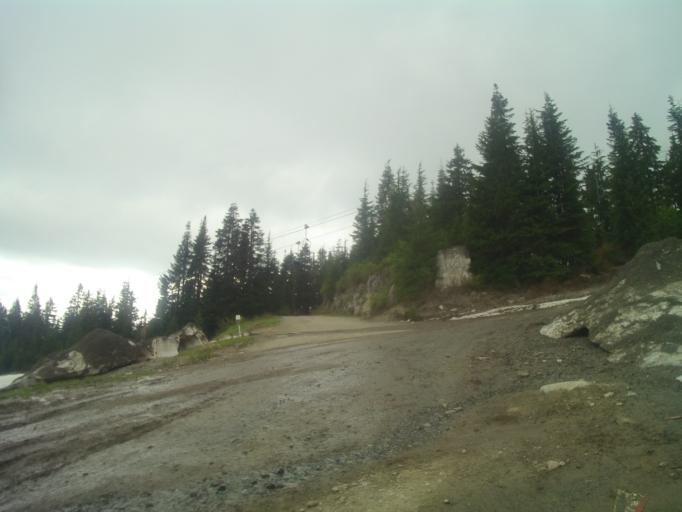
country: CA
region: British Columbia
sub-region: Fraser Valley Regional District
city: North Vancouver
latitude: 49.3792
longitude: -123.0797
